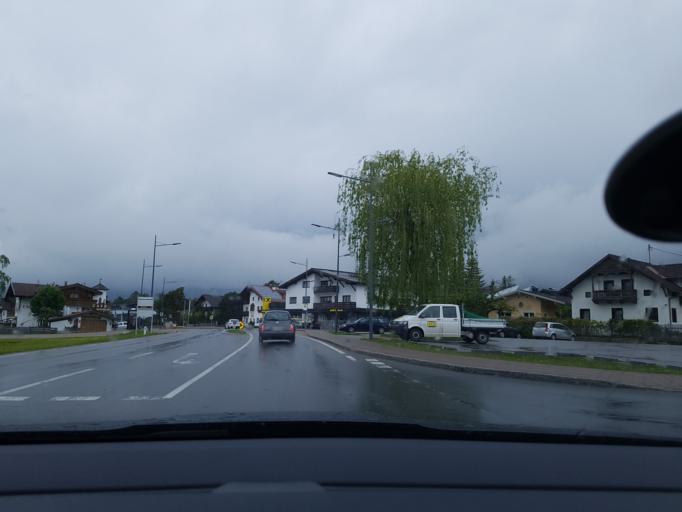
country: AT
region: Tyrol
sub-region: Politischer Bezirk Imst
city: Mieming
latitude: 47.3056
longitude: 10.9802
